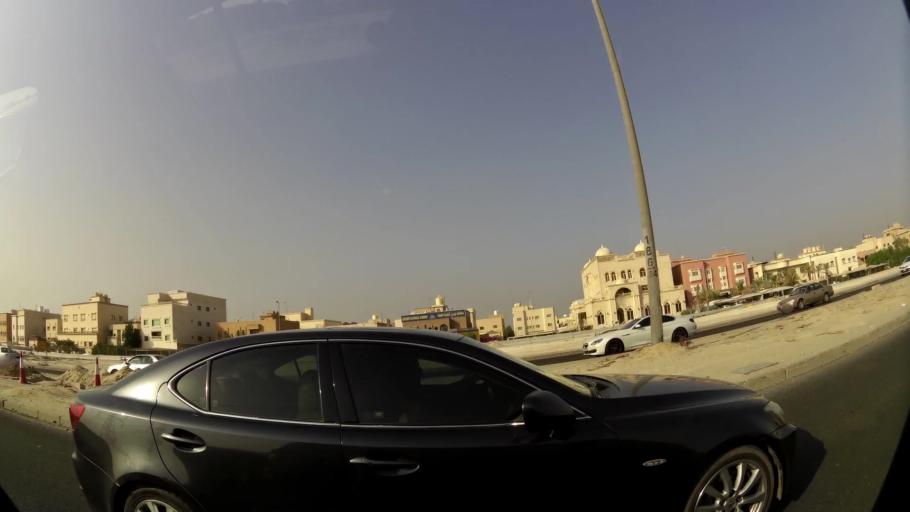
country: KW
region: Al Asimah
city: Ar Rabiyah
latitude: 29.2960
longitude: 47.8738
